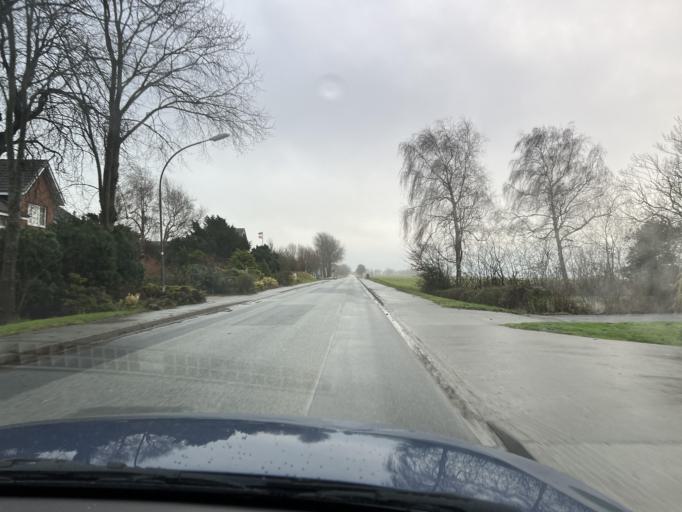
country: DE
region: Schleswig-Holstein
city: Norderwohrden
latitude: 54.2165
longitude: 9.0231
